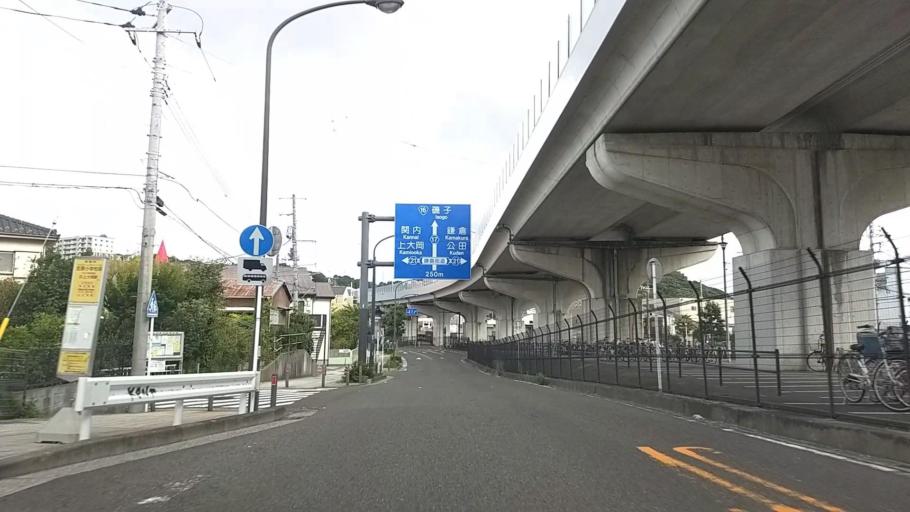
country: JP
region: Kanagawa
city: Yokohama
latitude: 35.3957
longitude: 139.5833
